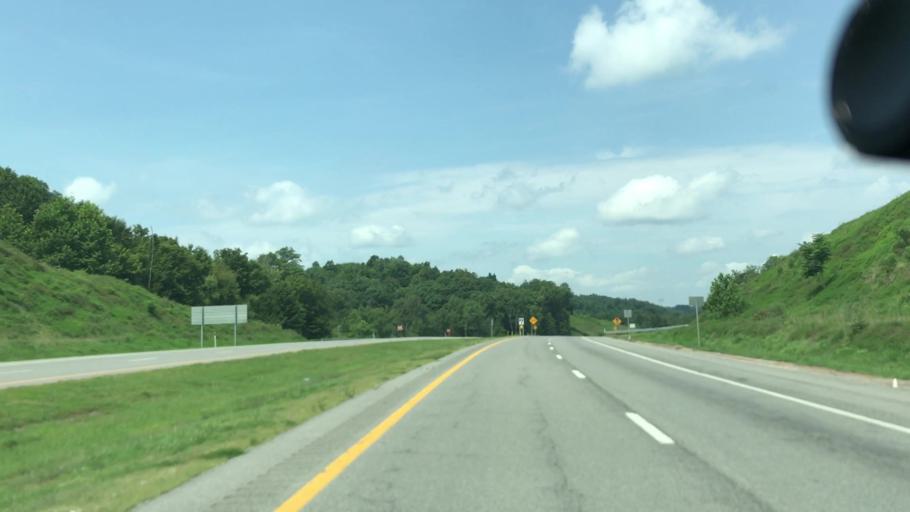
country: US
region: West Virginia
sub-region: Putnam County
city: Buffalo
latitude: 38.5597
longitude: -82.0087
